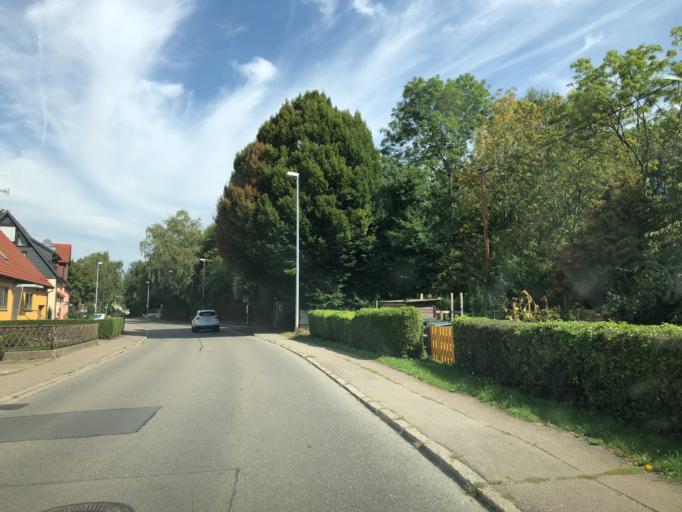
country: DE
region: Baden-Wuerttemberg
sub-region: Regierungsbezirk Stuttgart
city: Unterensingen
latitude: 48.6420
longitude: 9.3491
